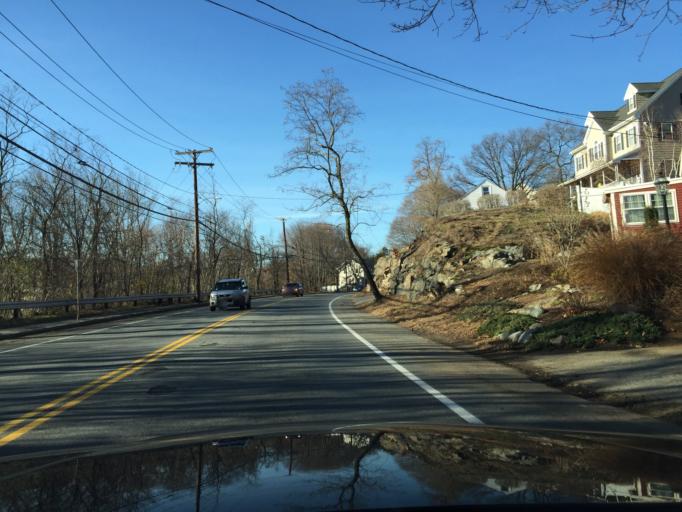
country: US
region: Massachusetts
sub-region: Middlesex County
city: Arlington
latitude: 42.4196
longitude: -71.1595
